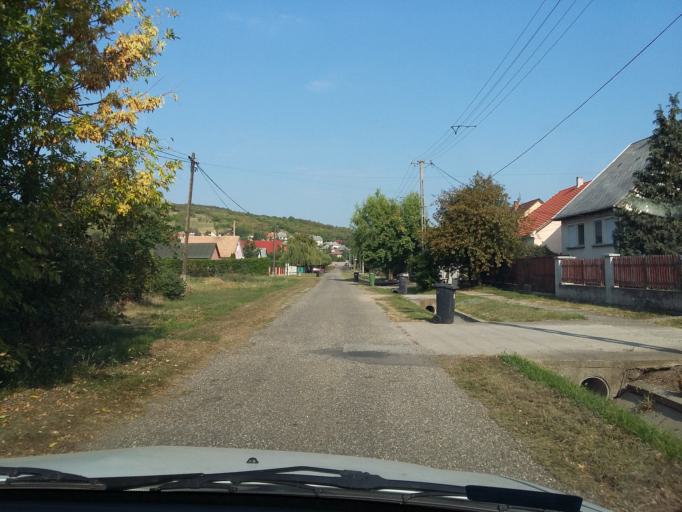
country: HU
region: Borsod-Abauj-Zemplen
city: Bekecs
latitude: 48.1499
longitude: 21.1793
